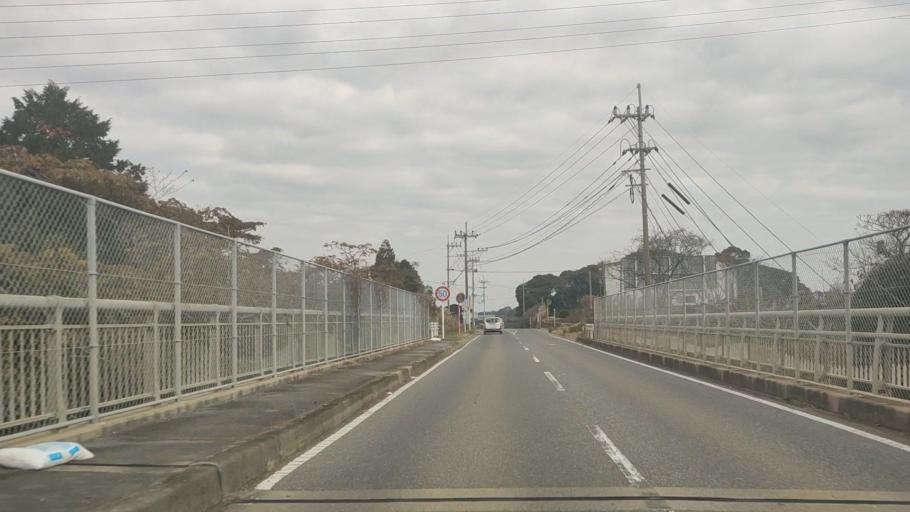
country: JP
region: Nagasaki
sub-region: Isahaya-shi
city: Isahaya
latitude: 32.8080
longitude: 130.1697
